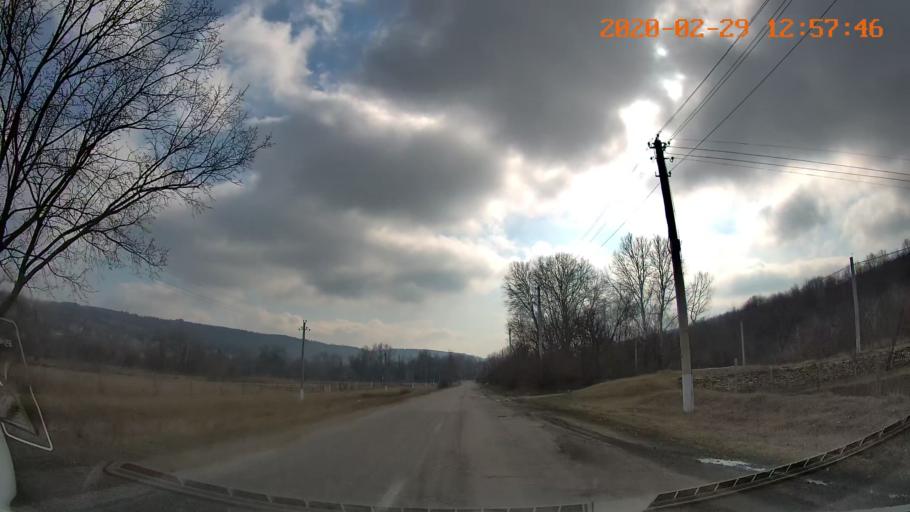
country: MD
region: Telenesti
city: Camenca
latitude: 48.0750
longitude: 28.7167
